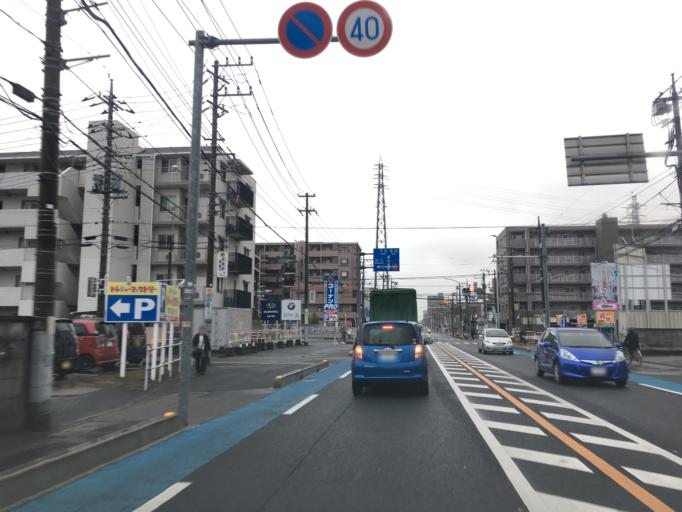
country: JP
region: Saitama
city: Koshigaya
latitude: 35.8828
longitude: 139.7925
